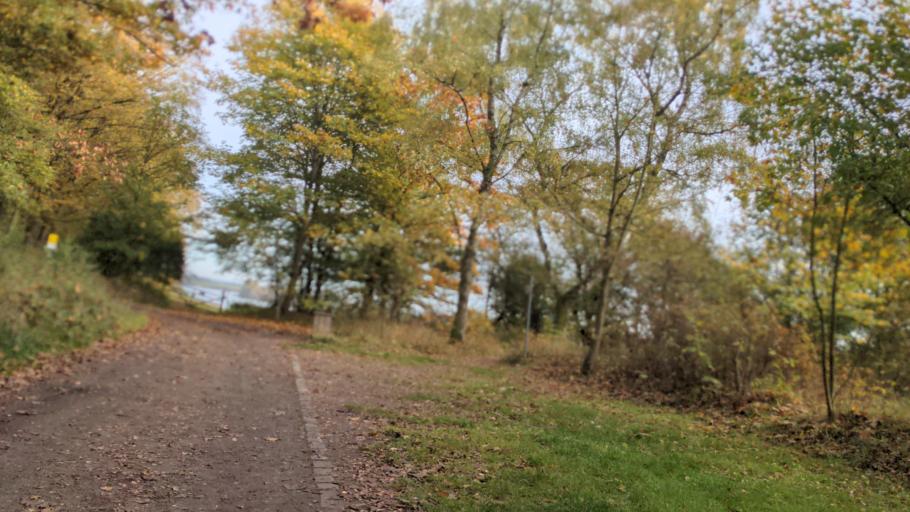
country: DE
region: Mecklenburg-Vorpommern
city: Selmsdorf
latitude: 53.9199
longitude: 10.8599
